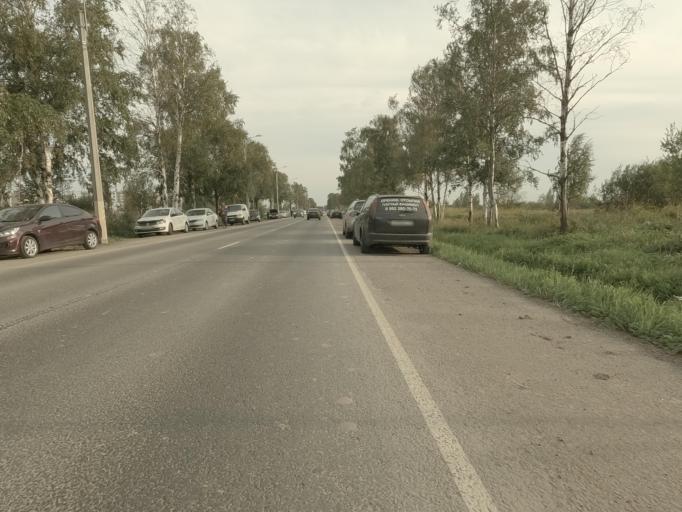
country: RU
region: St.-Petersburg
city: Strel'na
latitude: 59.8474
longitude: 30.0908
